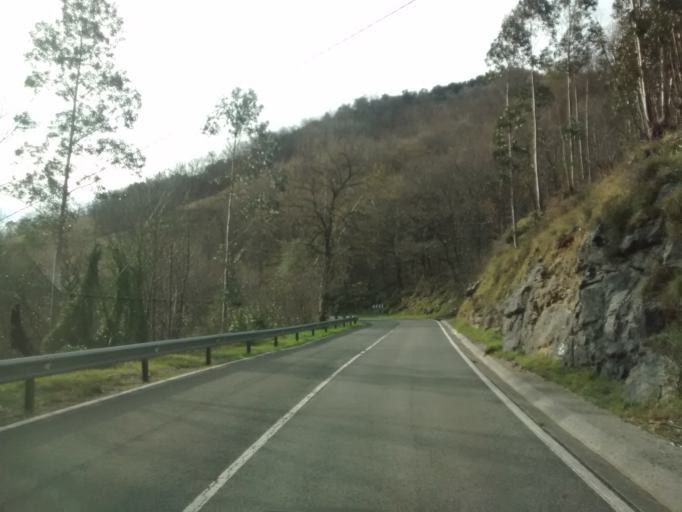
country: ES
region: Cantabria
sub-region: Provincia de Cantabria
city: Arredondo
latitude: 43.2800
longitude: -3.6159
